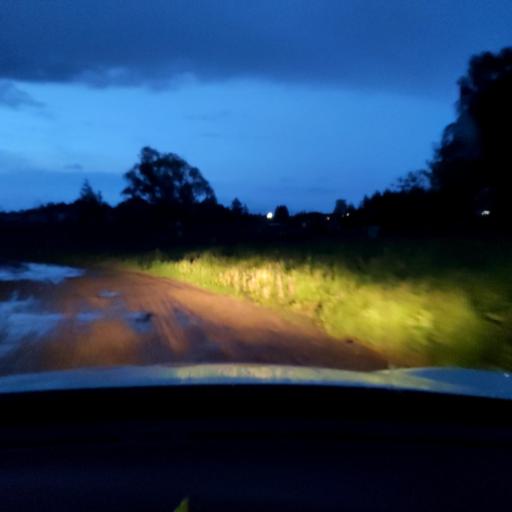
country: RU
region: Tatarstan
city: Stolbishchi
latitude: 55.6481
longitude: 49.2837
